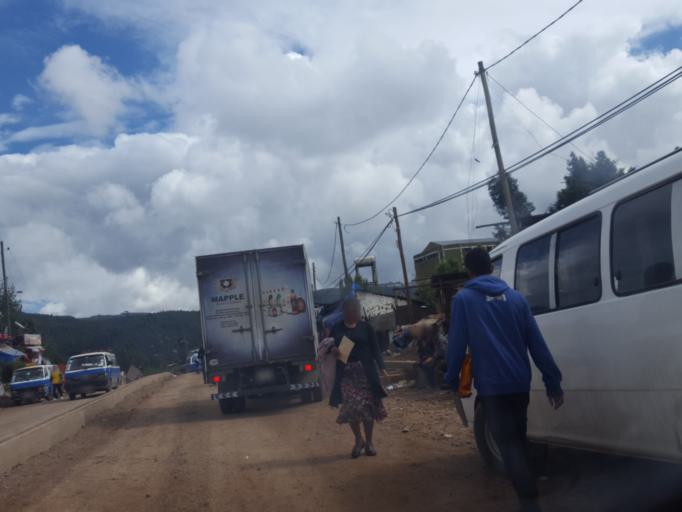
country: ET
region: Adis Abeba
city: Addis Ababa
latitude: 9.0644
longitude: 38.7620
